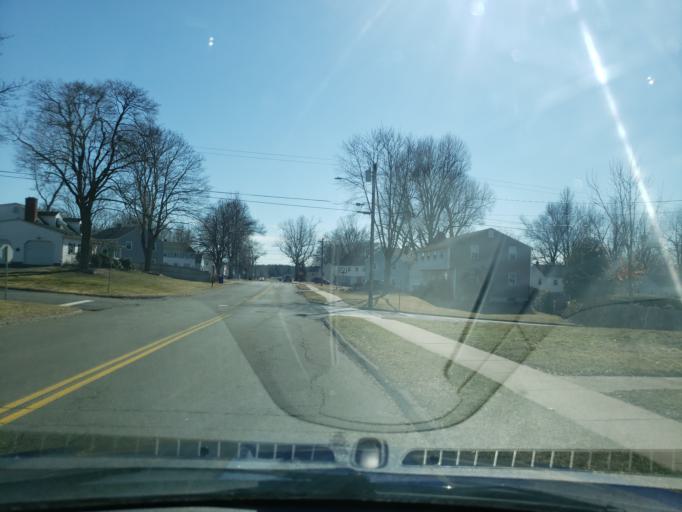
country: US
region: Connecticut
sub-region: Hartford County
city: Enfield
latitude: 41.9833
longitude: -72.5985
